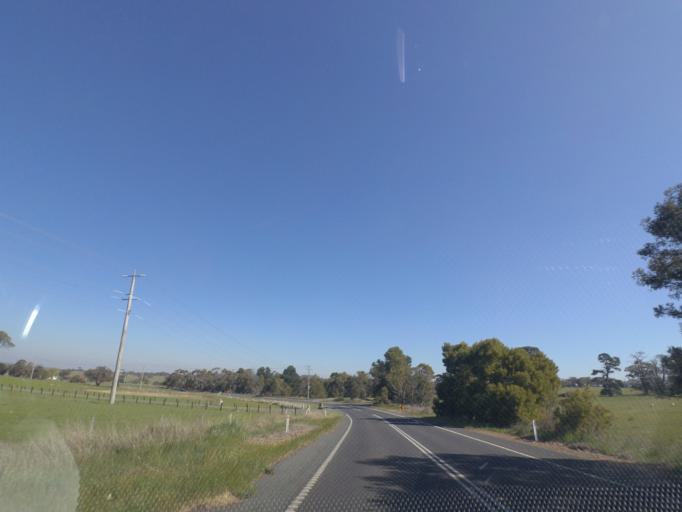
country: AU
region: Victoria
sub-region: Whittlesea
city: Whittlesea
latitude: -37.3357
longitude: 144.9828
